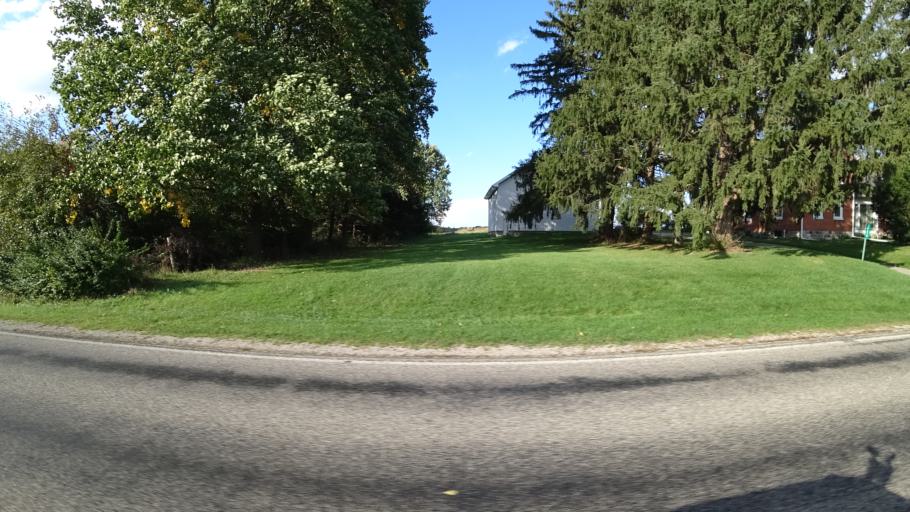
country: US
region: Michigan
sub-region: Saint Joseph County
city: Sturgis
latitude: 41.8540
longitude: -85.4300
